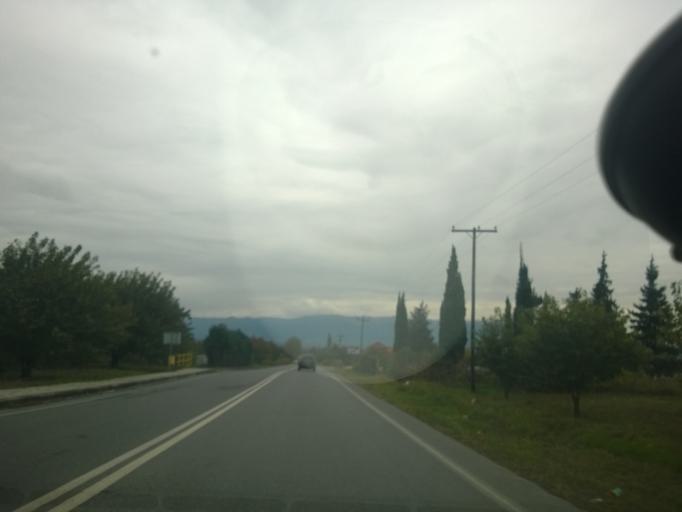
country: GR
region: Central Macedonia
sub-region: Nomos Pellis
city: Loutraki
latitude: 40.9708
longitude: 21.9541
